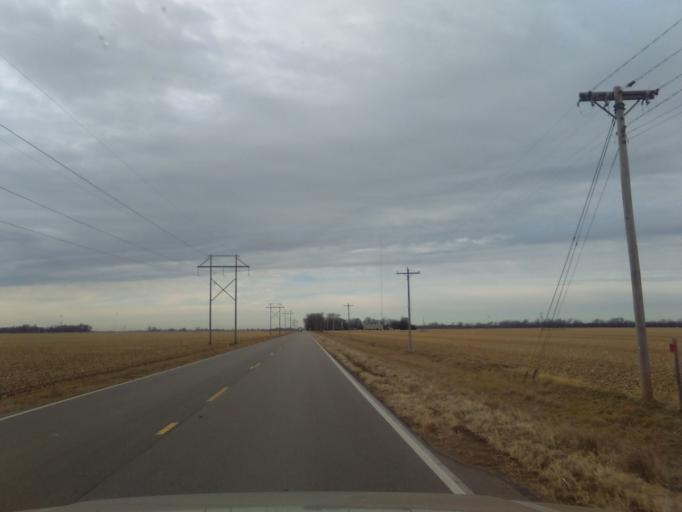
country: US
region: Nebraska
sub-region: Buffalo County
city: Gibbon
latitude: 40.6550
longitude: -98.8383
